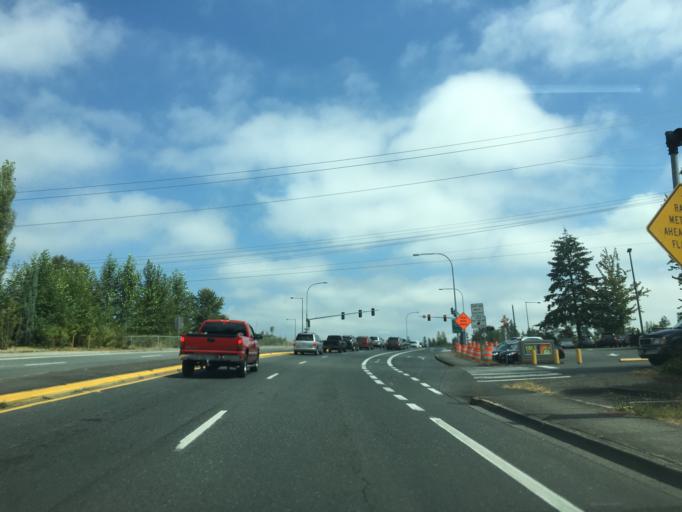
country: US
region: Washington
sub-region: King County
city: Kingsgate
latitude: 47.7412
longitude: -122.1889
